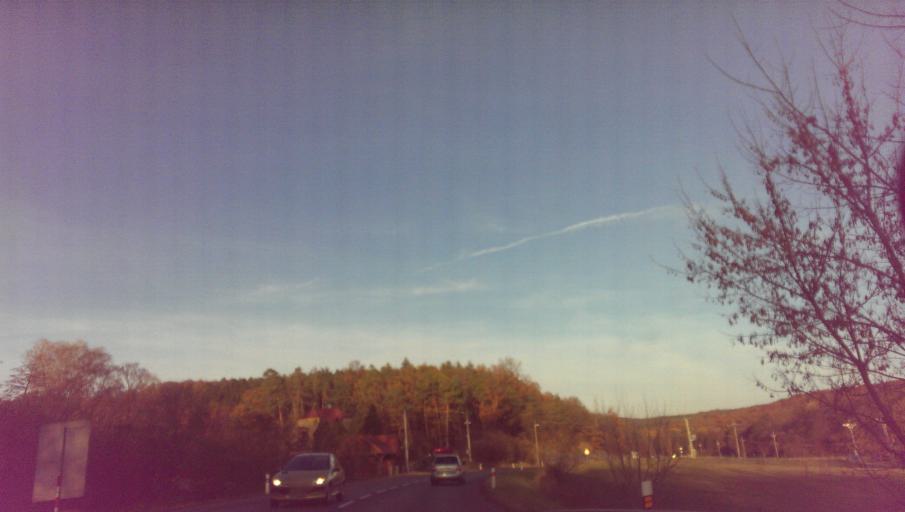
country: CZ
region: Zlin
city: Brezolupy
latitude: 49.1304
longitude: 17.5904
